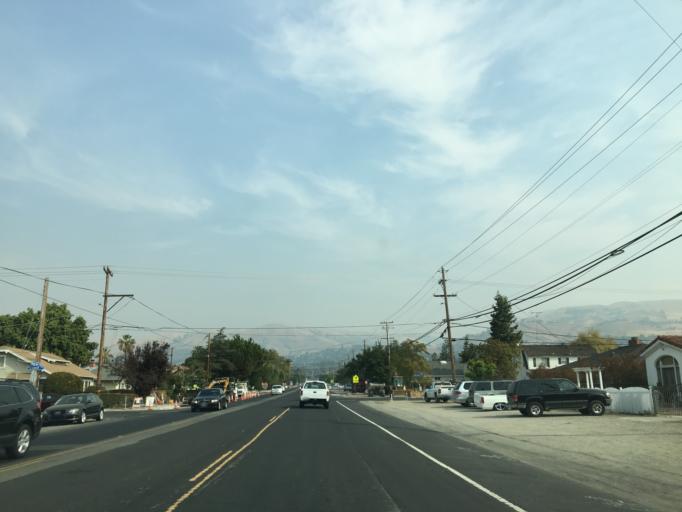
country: US
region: California
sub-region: Santa Clara County
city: Alum Rock
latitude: 37.3687
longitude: -121.8256
